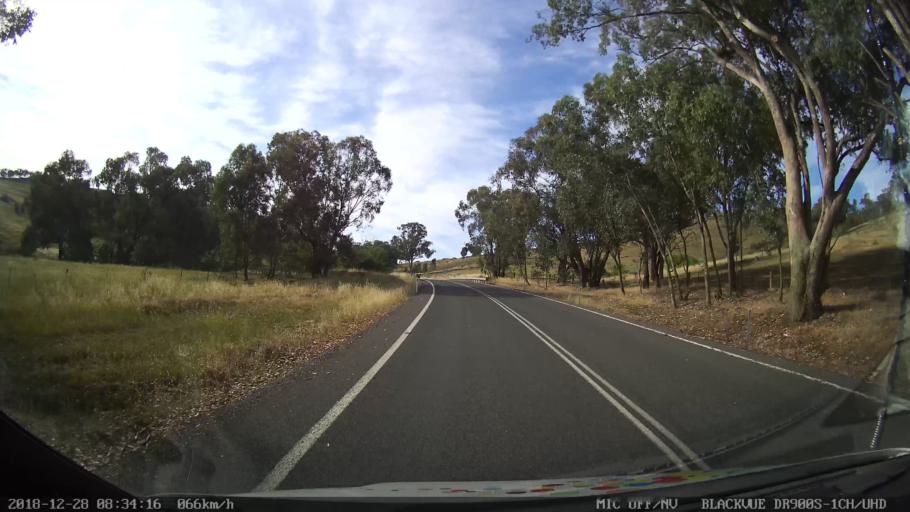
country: AU
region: New South Wales
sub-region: Blayney
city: Blayney
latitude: -33.9732
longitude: 149.3085
